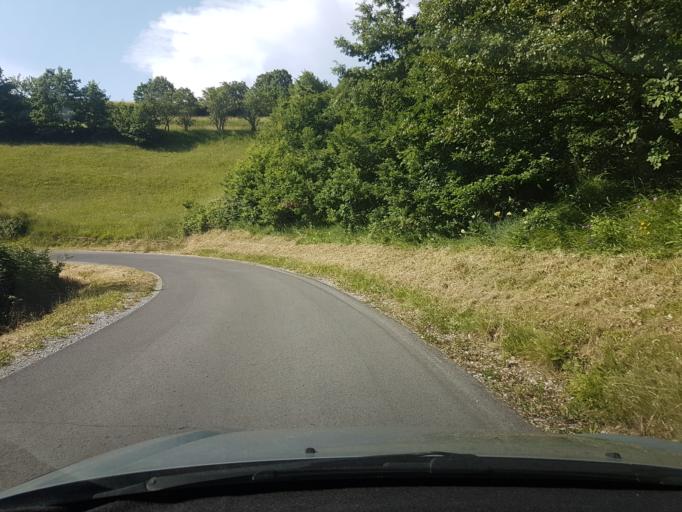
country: SI
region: Vipava
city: Vipava
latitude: 45.7694
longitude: 13.9700
